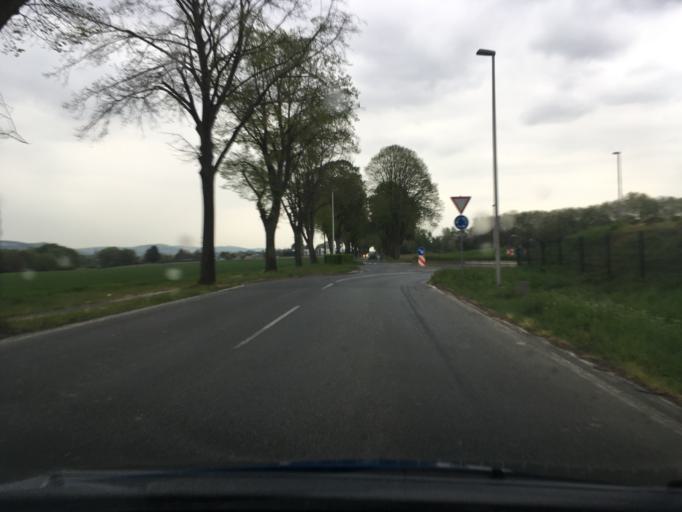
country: DE
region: Lower Saxony
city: Einbeck
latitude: 51.8260
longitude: 9.8419
